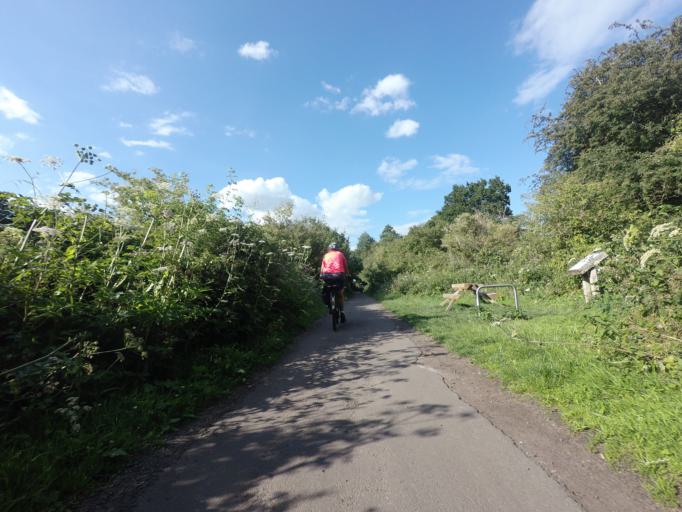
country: GB
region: England
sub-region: East Sussex
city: Hailsham
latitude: 50.8930
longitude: 0.2540
